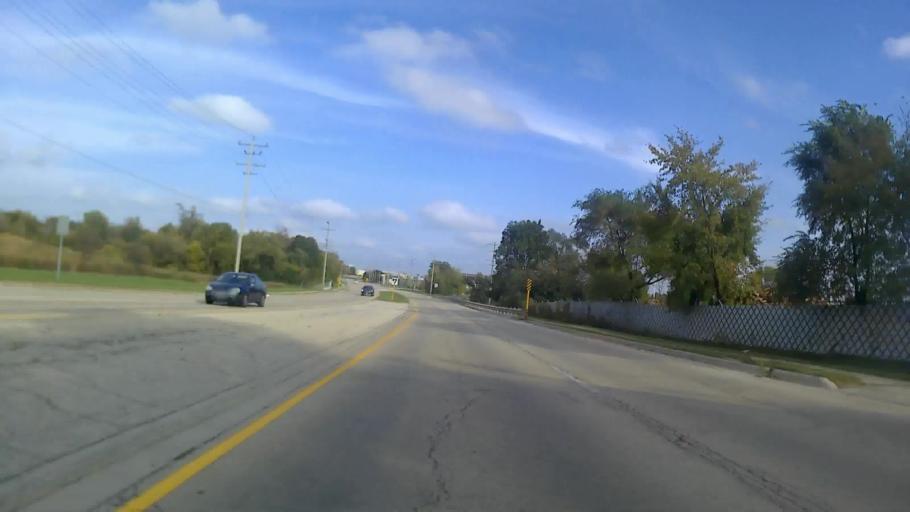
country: US
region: Illinois
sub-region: DuPage County
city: Warrenville
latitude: 41.8067
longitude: -88.1862
